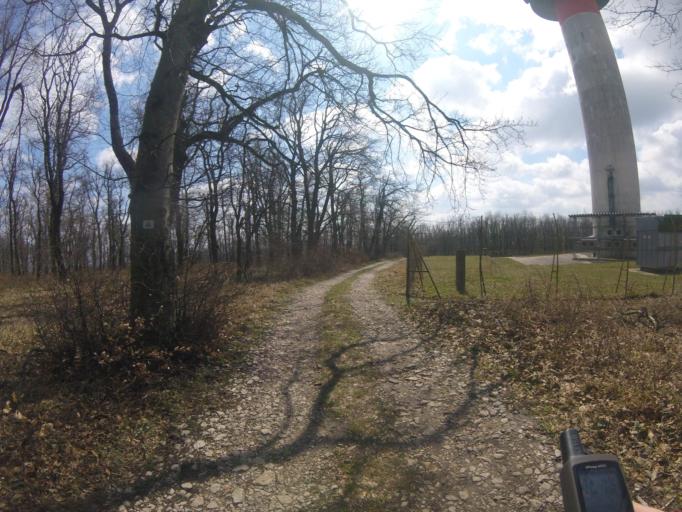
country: HU
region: Komarom-Esztergom
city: Tardos
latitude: 47.6766
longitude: 18.4942
